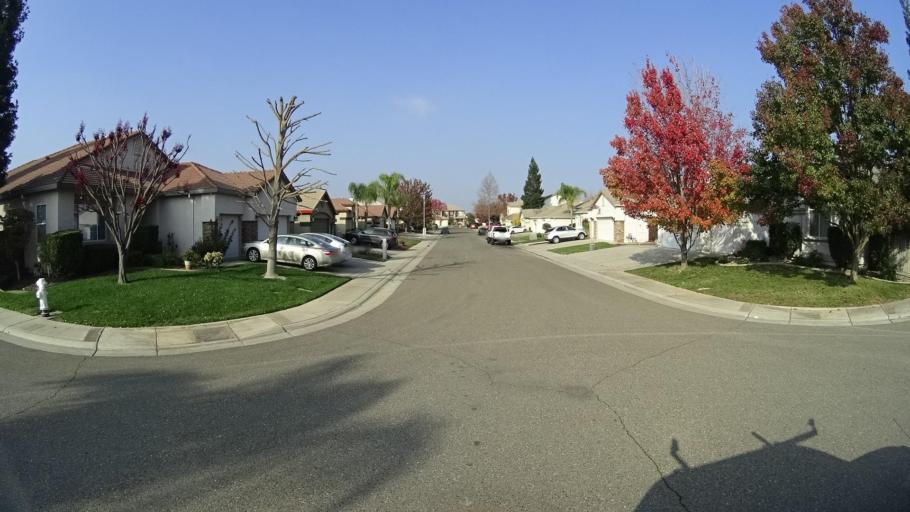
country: US
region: California
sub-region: Sacramento County
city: Elk Grove
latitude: 38.4109
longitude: -121.3372
